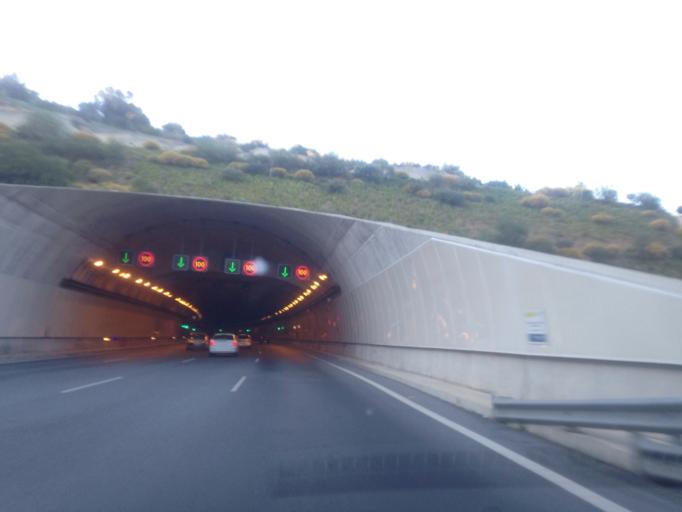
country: ES
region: Andalusia
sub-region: Provincia de Malaga
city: Torremolinos
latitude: 36.6488
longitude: -4.5126
